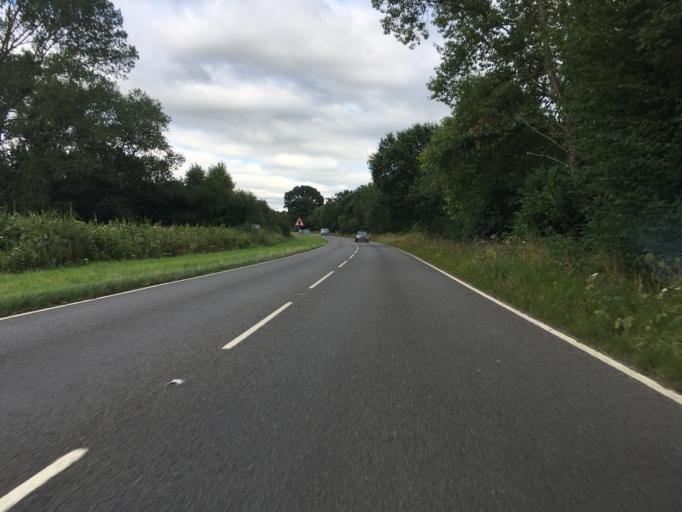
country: GB
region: England
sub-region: Hampshire
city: Liss
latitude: 51.0061
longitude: -0.8861
